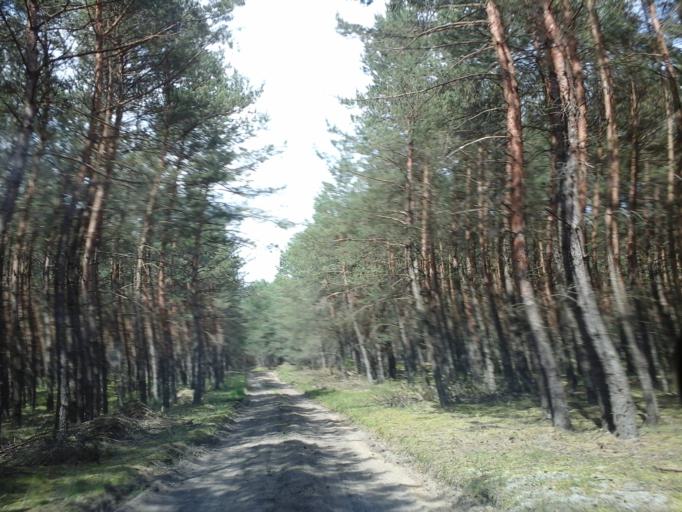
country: PL
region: West Pomeranian Voivodeship
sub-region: Powiat choszczenski
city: Drawno
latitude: 53.1346
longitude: 15.7654
